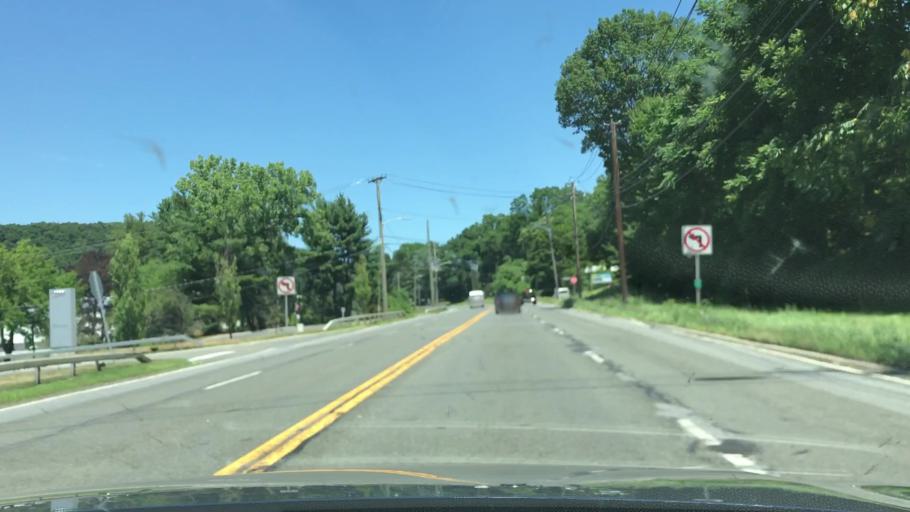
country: US
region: New York
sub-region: Westchester County
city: Hawthorne
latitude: 41.0979
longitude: -73.8083
